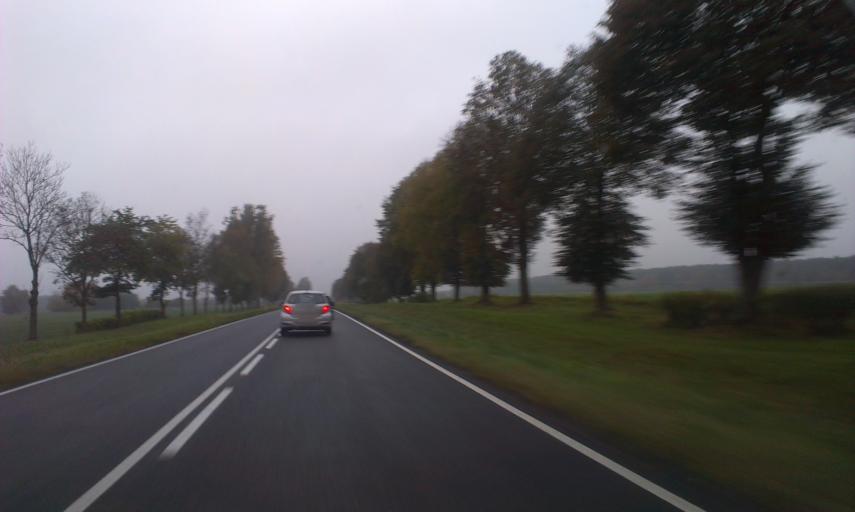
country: PL
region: West Pomeranian Voivodeship
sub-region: Powiat koszalinski
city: Bobolice
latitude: 54.0160
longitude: 16.4928
